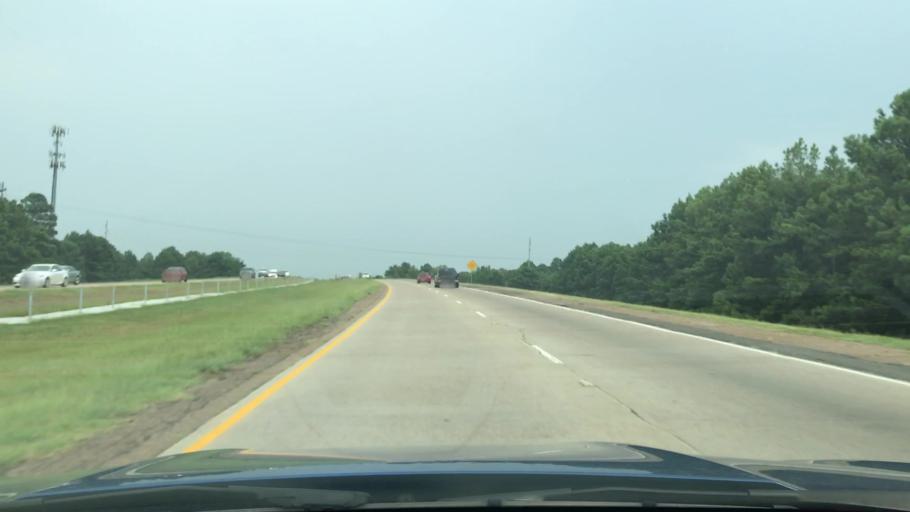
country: US
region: Louisiana
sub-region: Caddo Parish
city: Shreveport
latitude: 32.4210
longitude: -93.8335
